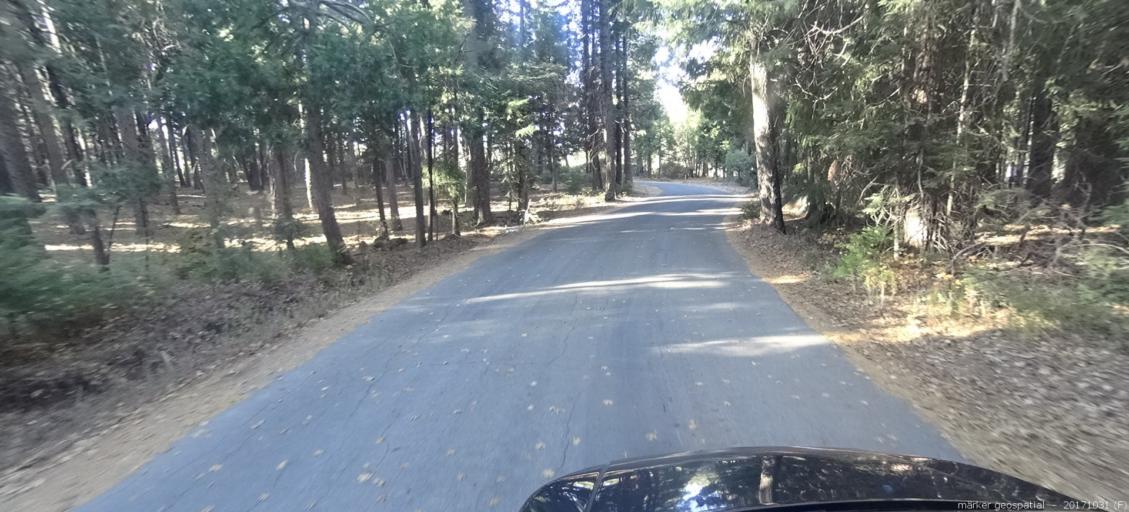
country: US
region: California
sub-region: Shasta County
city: Shingletown
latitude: 40.5248
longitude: -121.8360
